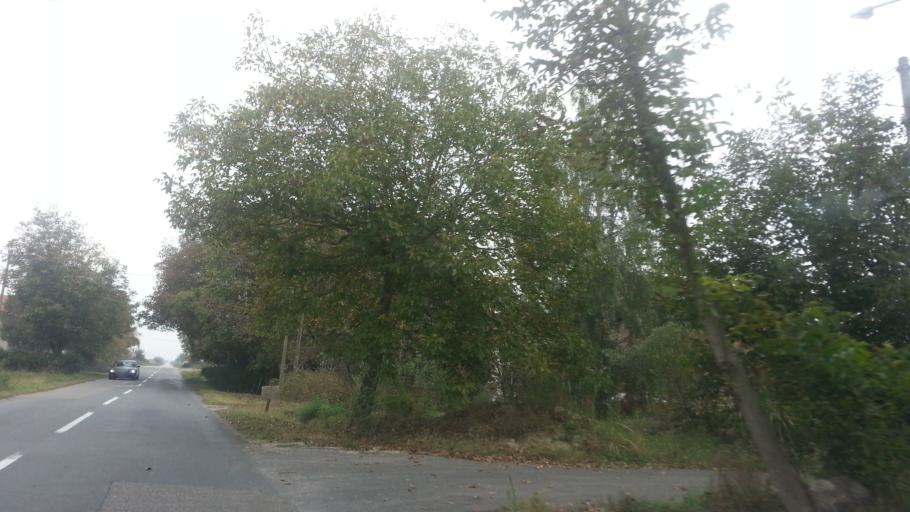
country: RS
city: Belegis
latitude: 45.0265
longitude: 20.3351
